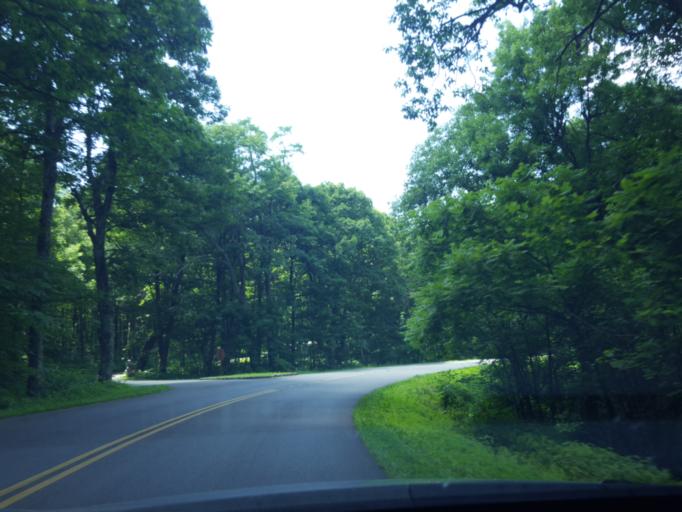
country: US
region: Virginia
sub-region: Nelson County
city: Nellysford
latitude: 37.9478
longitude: -78.9221
